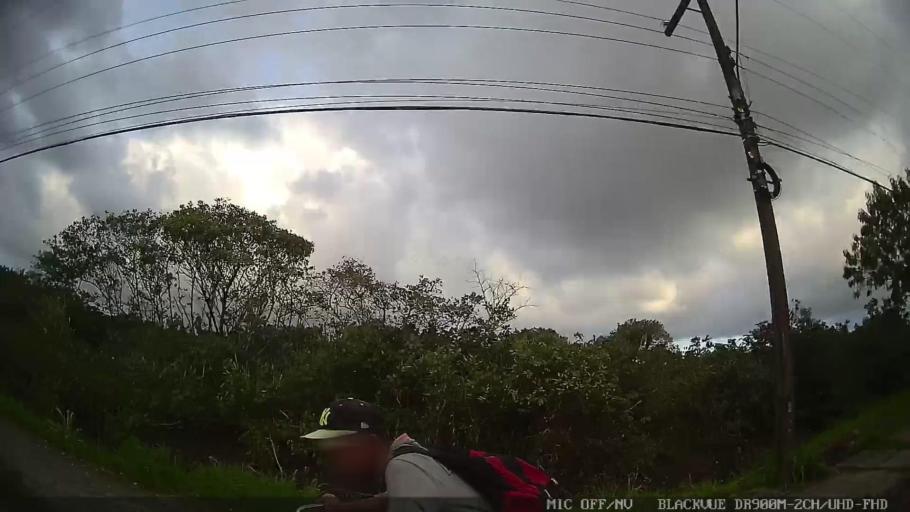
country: BR
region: Sao Paulo
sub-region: Itanhaem
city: Itanhaem
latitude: -24.1717
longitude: -46.7861
